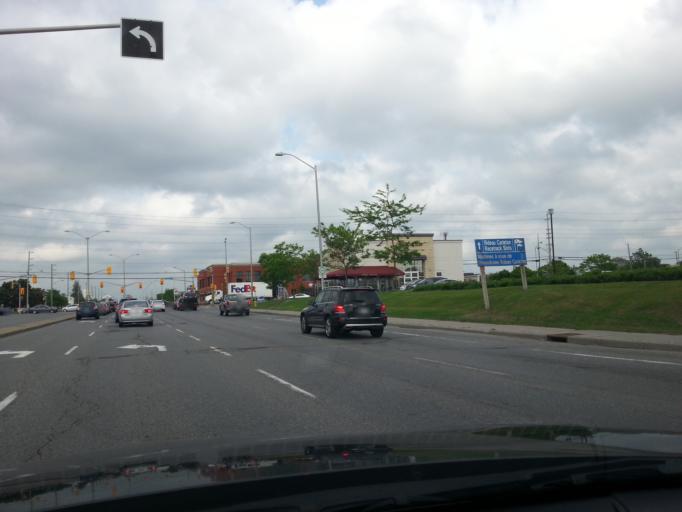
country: CA
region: Ontario
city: Ottawa
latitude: 45.3342
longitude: -75.7253
